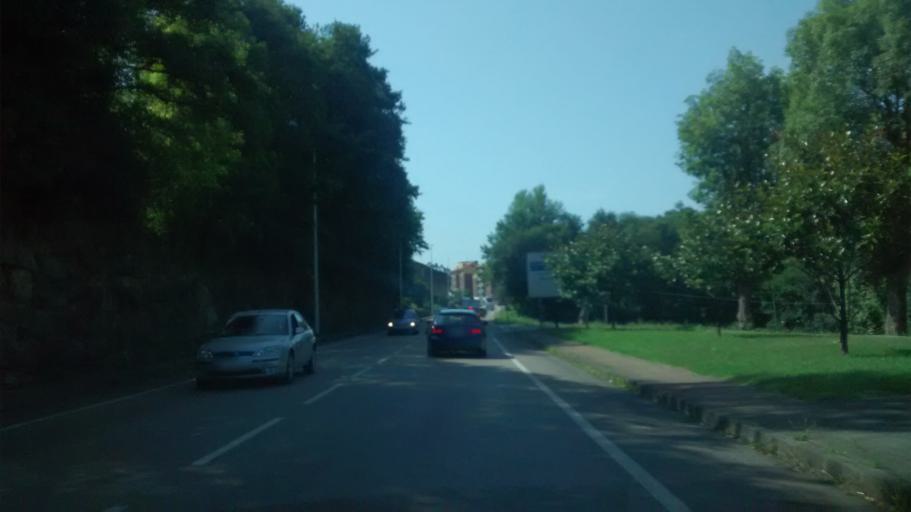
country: ES
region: Cantabria
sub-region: Provincia de Cantabria
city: Hazas de Cesto
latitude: 43.4185
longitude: -3.5746
